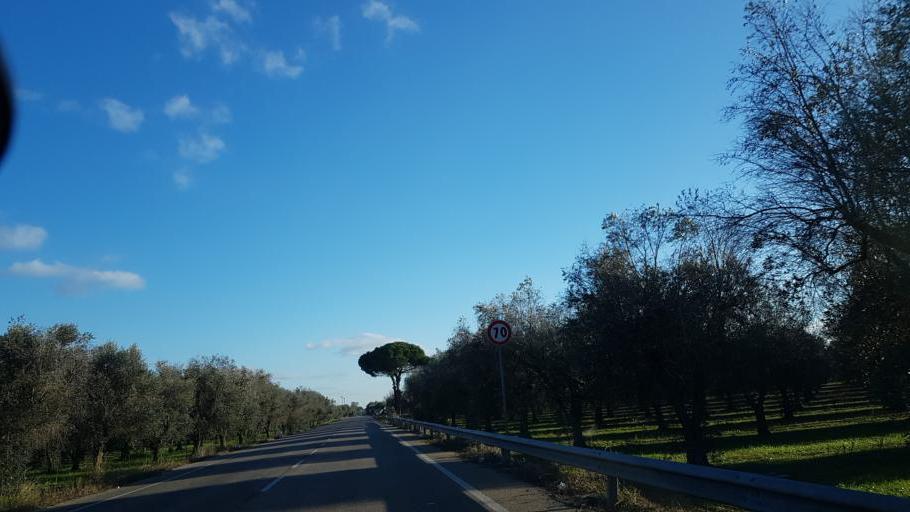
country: IT
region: Apulia
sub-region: Provincia di Lecce
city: Squinzano
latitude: 40.4527
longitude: 18.0267
